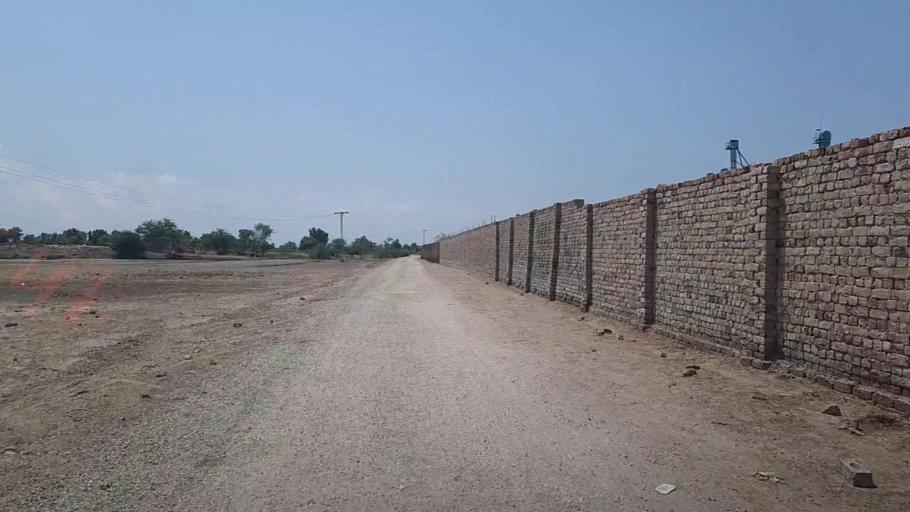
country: PK
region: Sindh
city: Ubauro
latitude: 28.1720
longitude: 69.7627
